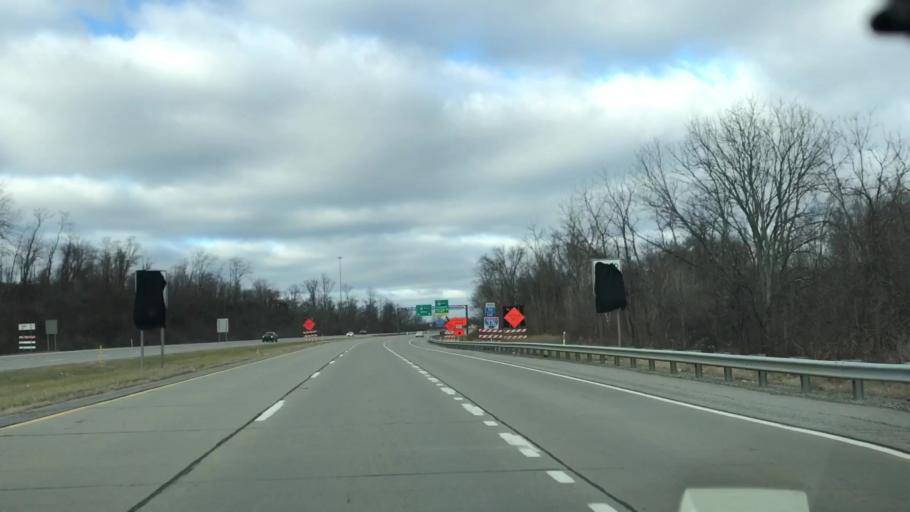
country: US
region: Pennsylvania
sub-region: Allegheny County
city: Carnot-Moon
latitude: 40.5104
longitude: -80.2620
